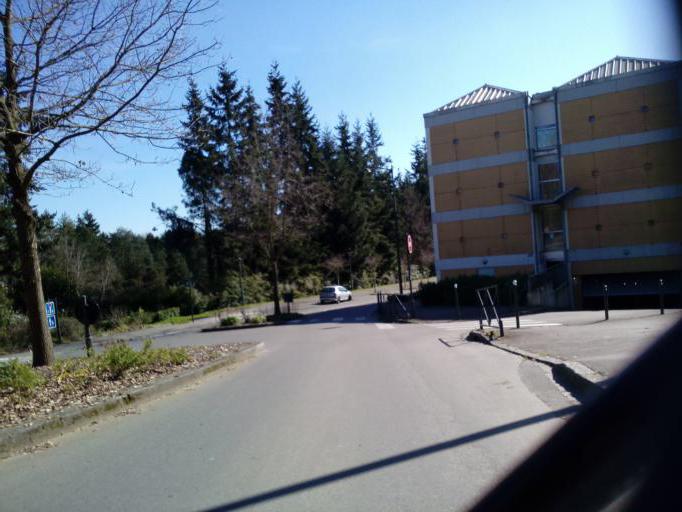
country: FR
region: Brittany
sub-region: Departement d'Ille-et-Vilaine
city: Rennes
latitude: 48.1258
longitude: -1.6413
